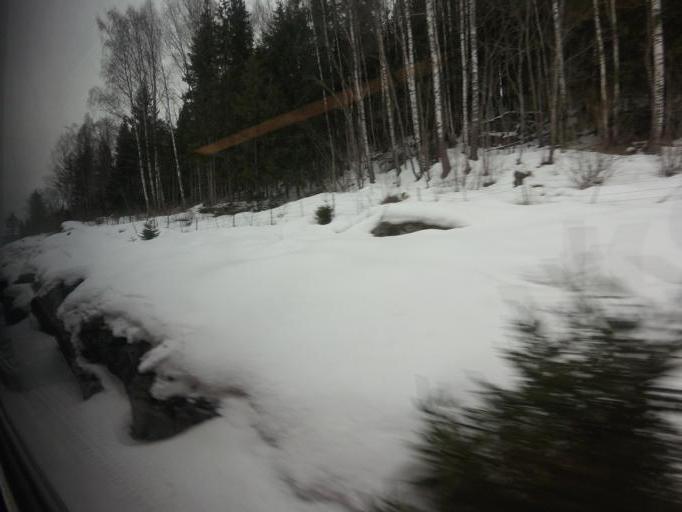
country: NO
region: Oppland
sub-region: Lillehammer
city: Lillehammer
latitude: 61.0696
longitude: 10.4564
